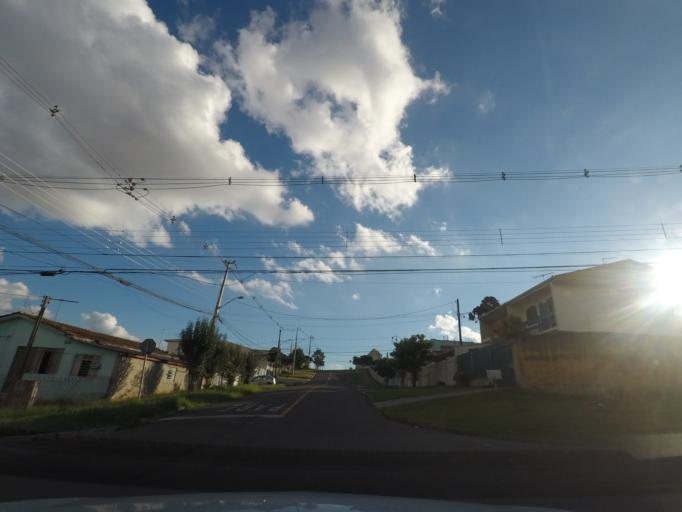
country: BR
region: Parana
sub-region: Sao Jose Dos Pinhais
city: Sao Jose dos Pinhais
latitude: -25.4958
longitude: -49.2570
